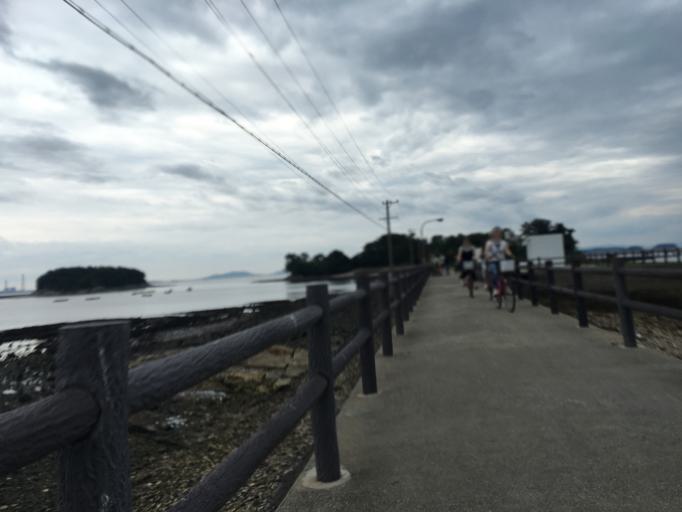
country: JP
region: Aichi
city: Ishiki
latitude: 34.7199
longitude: 137.0464
